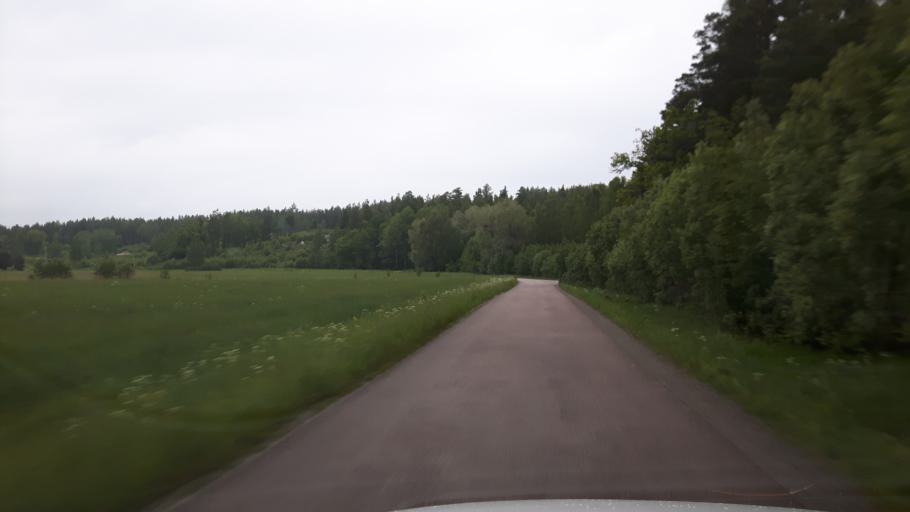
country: SE
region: Vaestmanland
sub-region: Arboga Kommun
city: Tyringe
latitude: 59.3902
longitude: 15.9436
